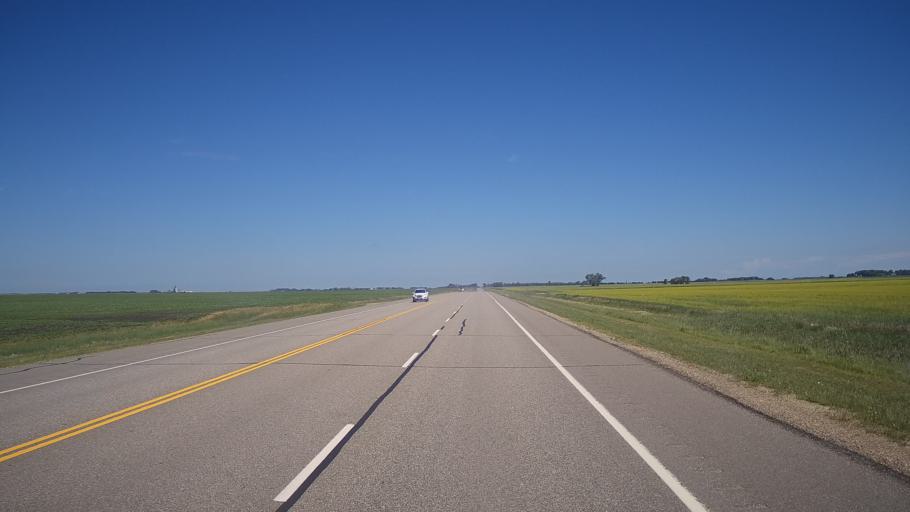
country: CA
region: Manitoba
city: Portage la Prairie
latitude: 50.0225
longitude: -98.4689
